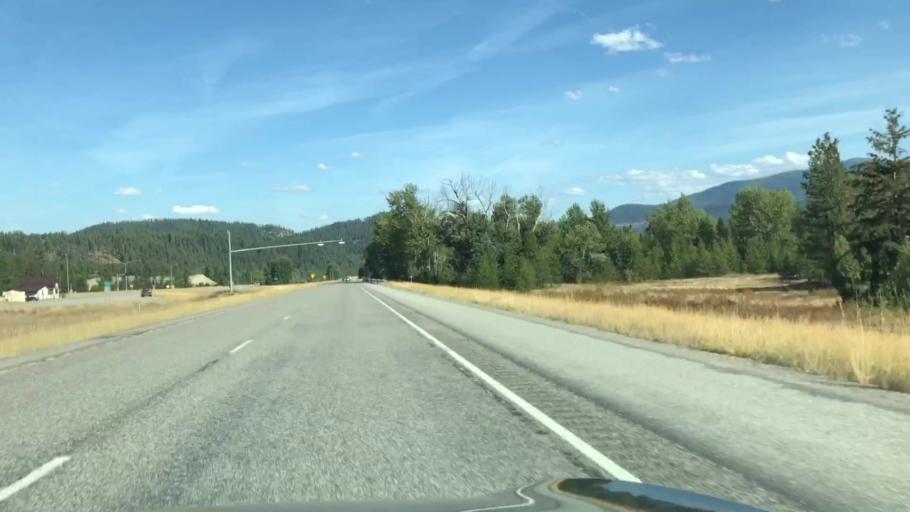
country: US
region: Montana
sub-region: Sanders County
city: Thompson Falls
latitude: 47.3935
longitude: -115.4267
